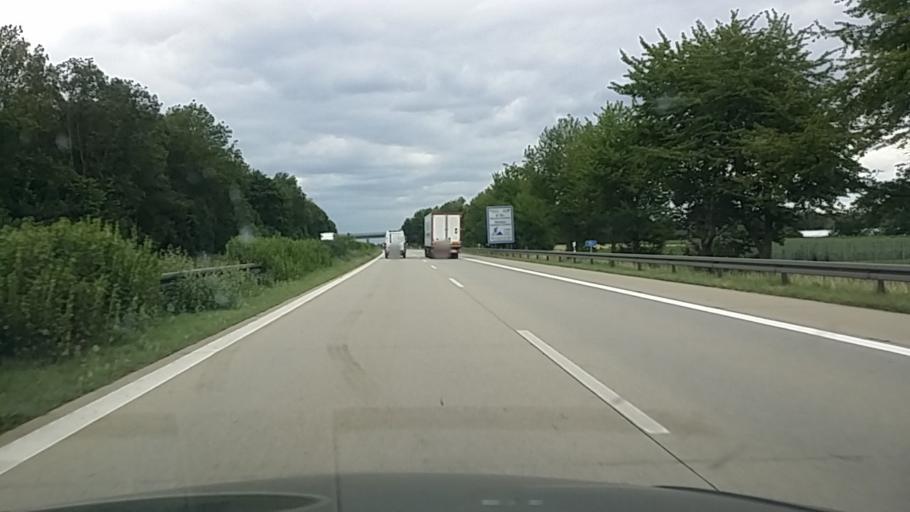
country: DE
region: Bavaria
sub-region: Lower Bavaria
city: Essenbach
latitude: 48.5895
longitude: 12.2060
